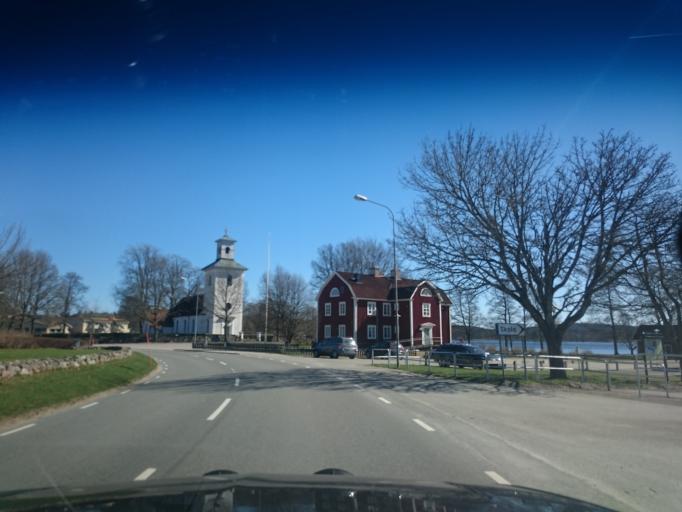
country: SE
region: Joenkoeping
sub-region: Vetlanda Kommun
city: Landsbro
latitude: 57.2048
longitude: 14.9483
